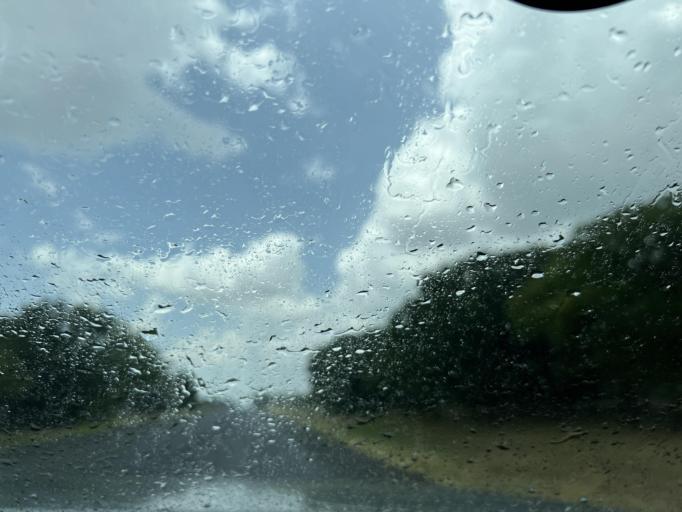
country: US
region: Texas
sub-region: Wise County
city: Boyd
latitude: 33.1177
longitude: -97.6547
